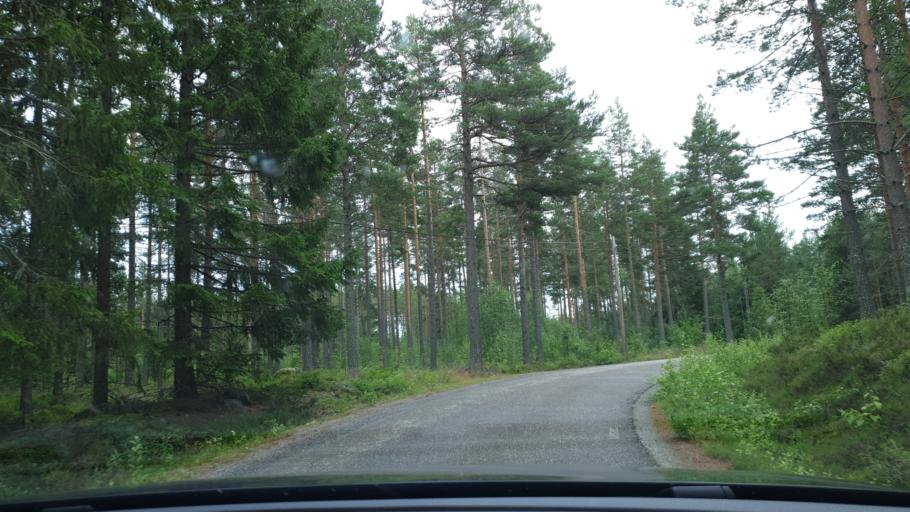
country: SE
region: Gaevleborg
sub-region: Hudiksvalls Kommun
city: Iggesund
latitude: 61.5358
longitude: 17.0104
